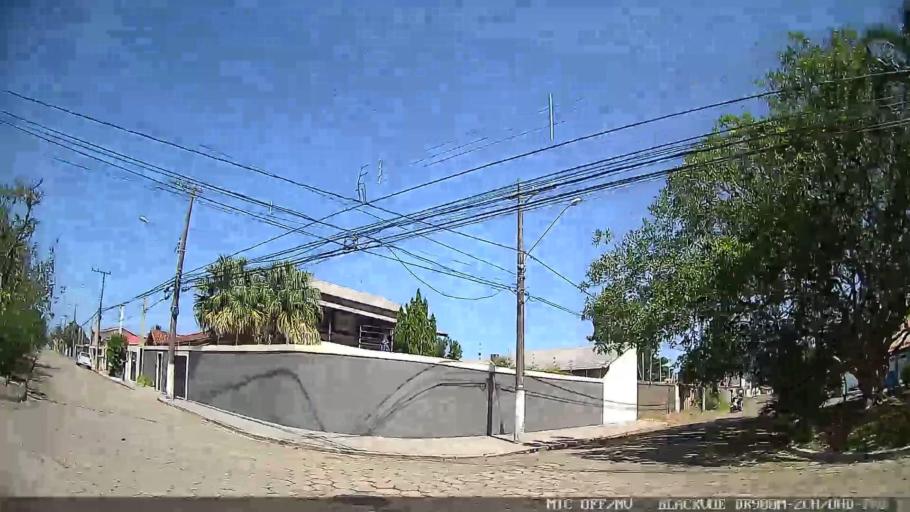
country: BR
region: Sao Paulo
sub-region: Peruibe
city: Peruibe
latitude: -24.2998
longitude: -46.9791
